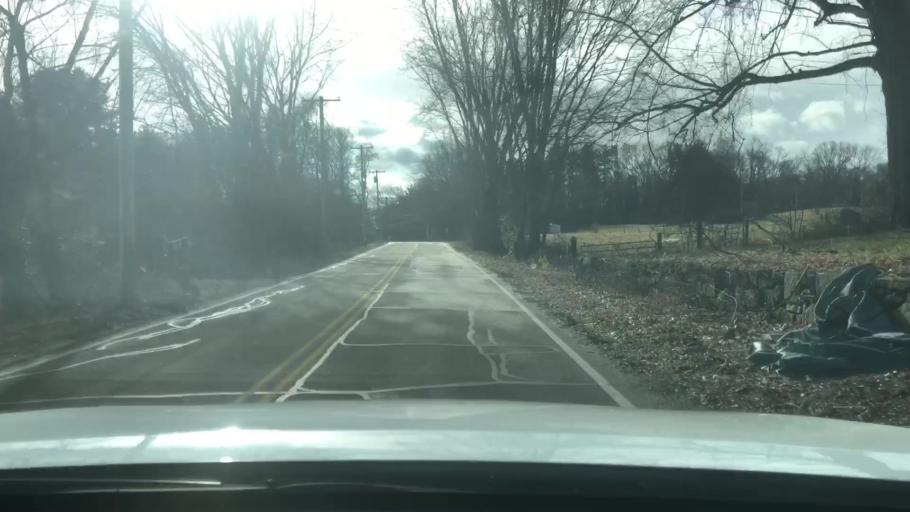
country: US
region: Massachusetts
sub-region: Worcester County
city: Blackstone
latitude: 42.0270
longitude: -71.5251
